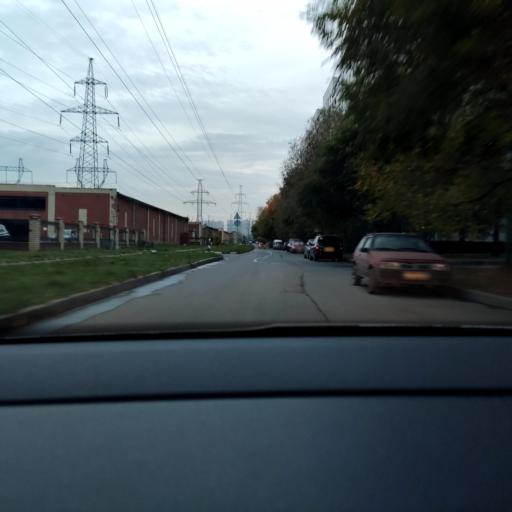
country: RU
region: Moscow
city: Bibirevo
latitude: 55.8859
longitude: 37.6143
